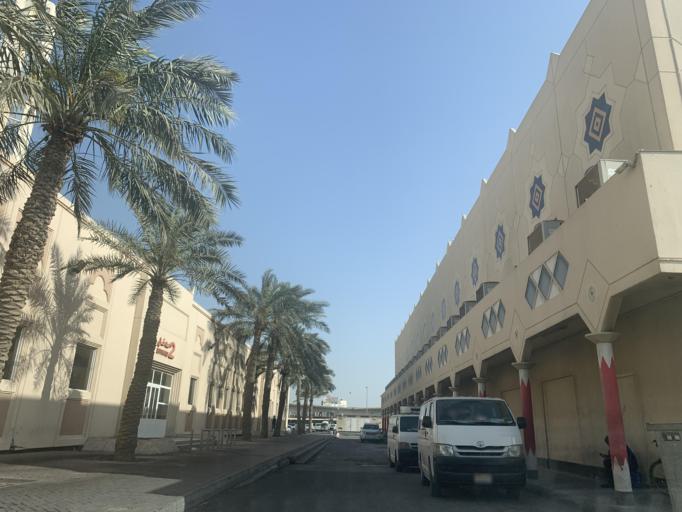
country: BH
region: Manama
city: Jidd Hafs
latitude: 26.2317
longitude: 50.5646
